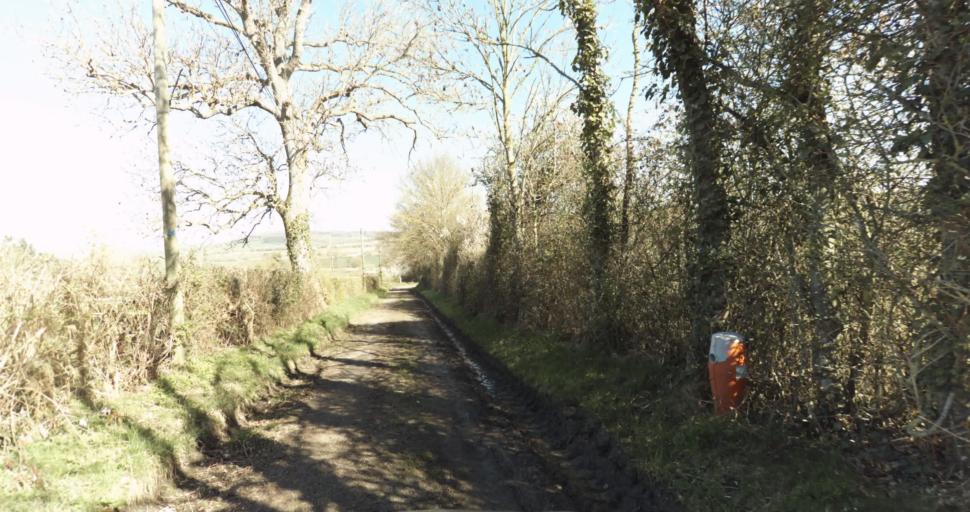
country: FR
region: Lower Normandy
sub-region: Departement du Calvados
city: Livarot
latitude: 48.9490
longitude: 0.0586
